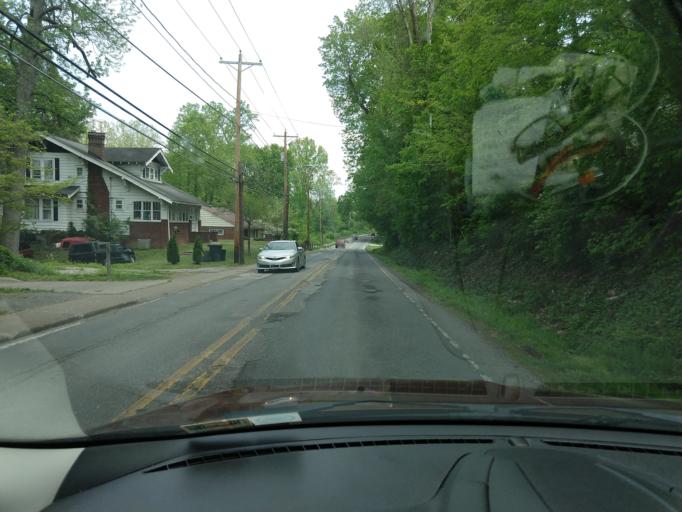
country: US
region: West Virginia
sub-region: Kanawha County
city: Saint Albans
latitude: 38.3761
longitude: -81.7996
